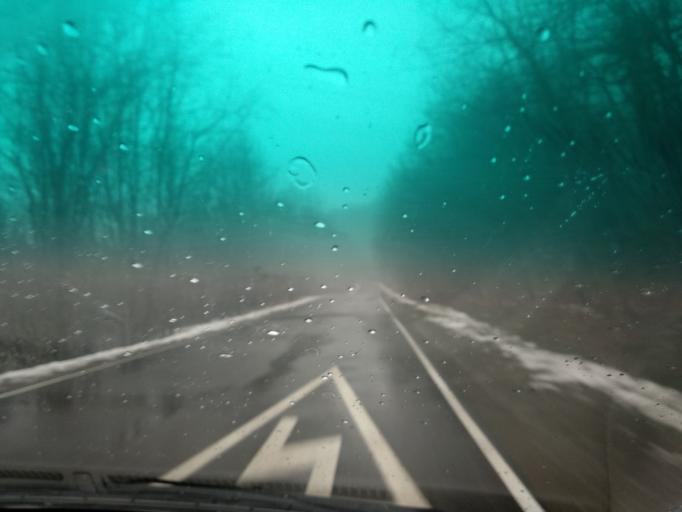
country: RU
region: Krasnodarskiy
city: Khadyzhensk
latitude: 44.2658
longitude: 39.3510
